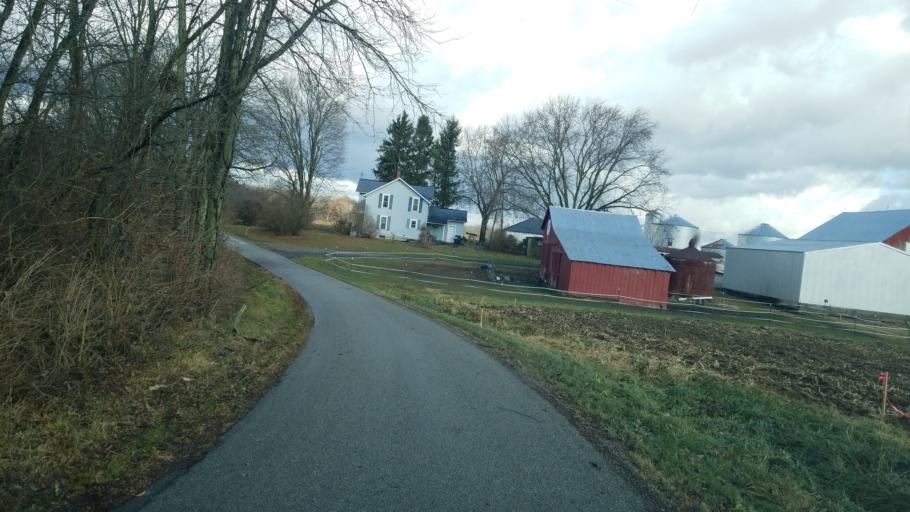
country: US
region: Ohio
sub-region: Marion County
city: Marion
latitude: 40.5342
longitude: -83.0379
